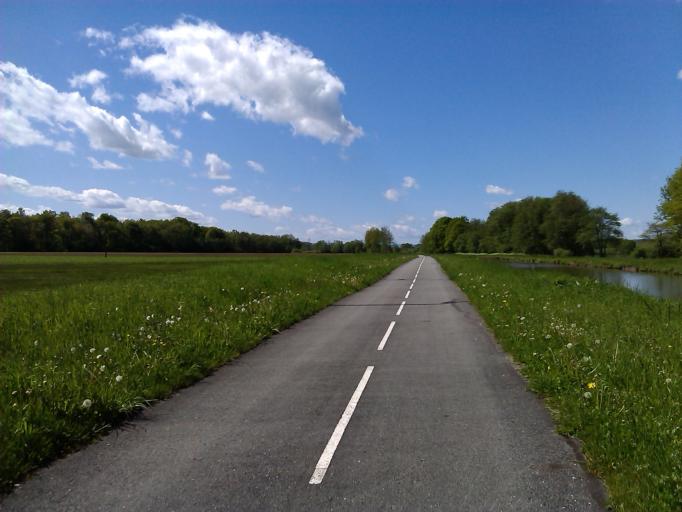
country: FR
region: Franche-Comte
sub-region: Territoire de Belfort
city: Morvillars
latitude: 47.5774
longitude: 6.9590
